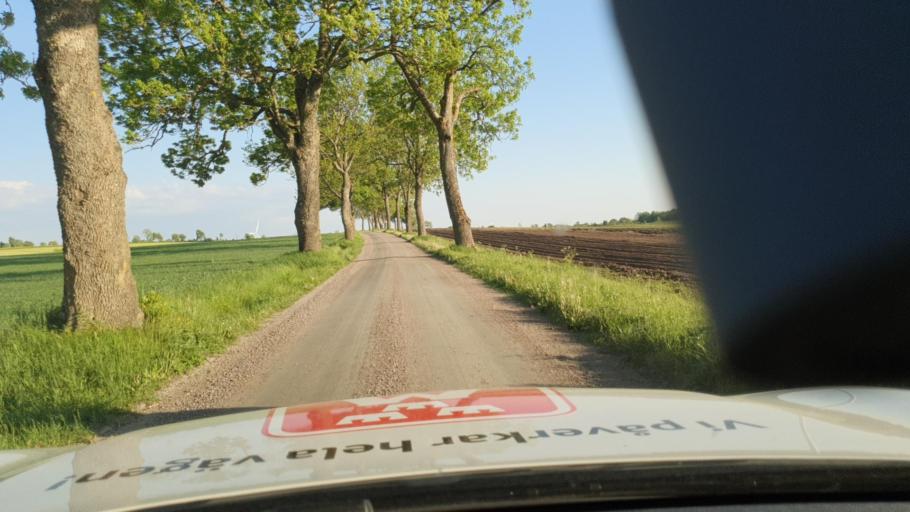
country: SE
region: Vaestra Goetaland
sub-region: Falkopings Kommun
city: Akarp
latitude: 58.1437
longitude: 13.6997
